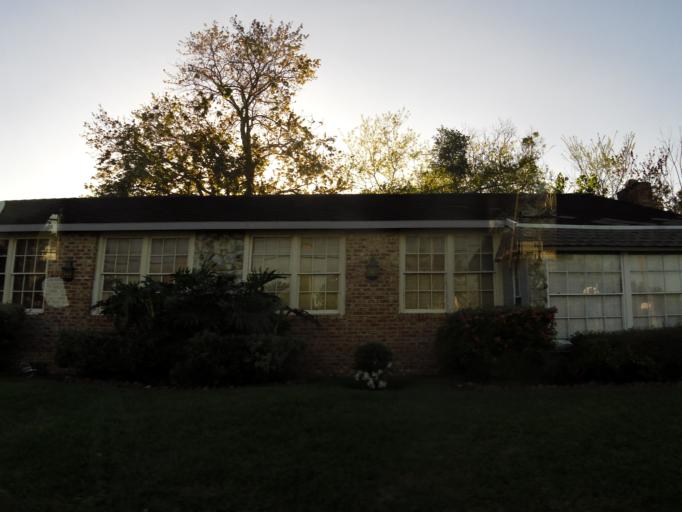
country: US
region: Florida
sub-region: Duval County
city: Jacksonville
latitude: 30.3382
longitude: -81.6973
